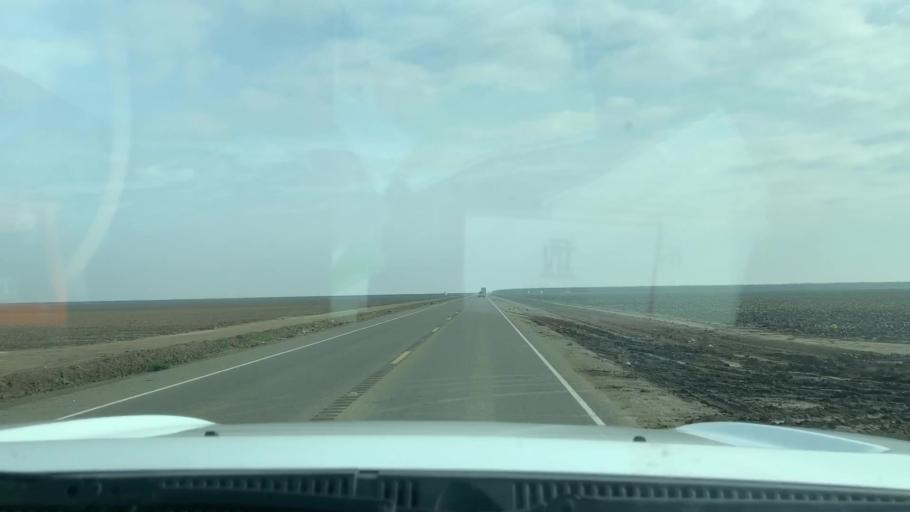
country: US
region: California
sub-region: Fresno County
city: Huron
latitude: 36.2554
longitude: -120.0216
